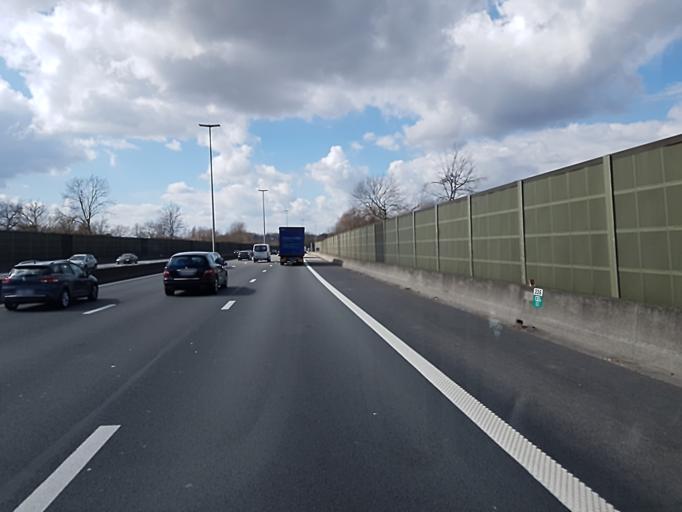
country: BE
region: Flanders
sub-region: Provincie Oost-Vlaanderen
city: Haaltert
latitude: 50.9265
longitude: 3.9760
